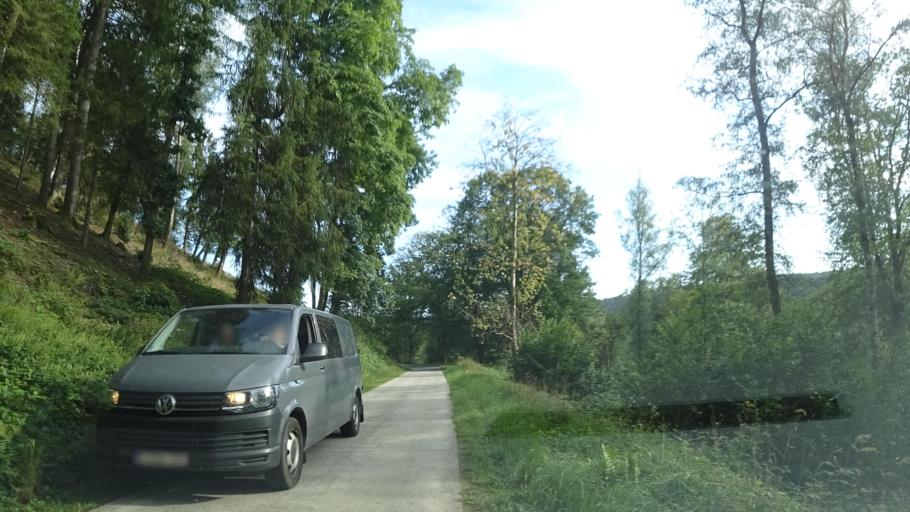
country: BE
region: Wallonia
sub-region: Province du Luxembourg
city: Herbeumont
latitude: 49.7697
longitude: 5.2495
